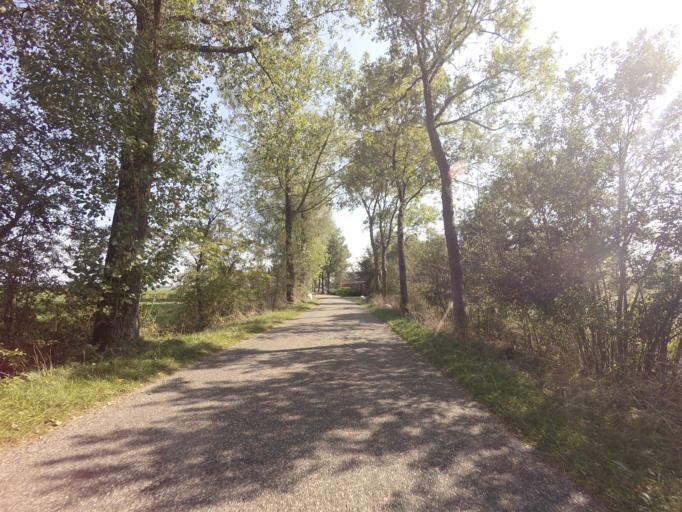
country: NL
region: Groningen
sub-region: Gemeente Zuidhorn
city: Zuidhorn
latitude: 53.2393
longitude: 6.4118
